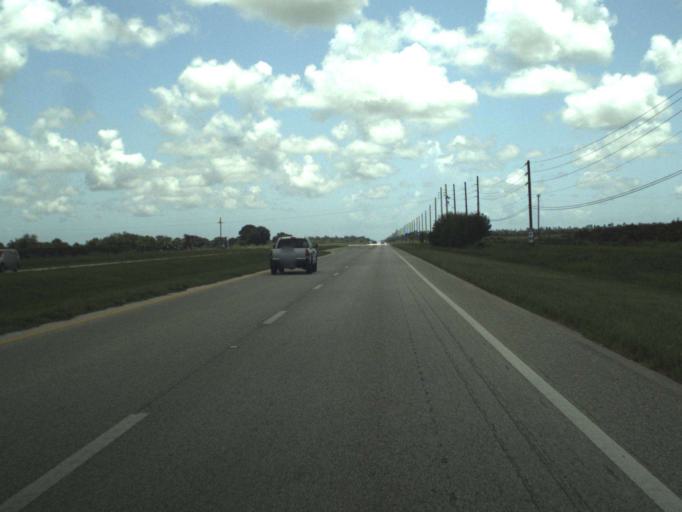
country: US
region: Florida
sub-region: Indian River County
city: West Vero Corridor
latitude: 27.6398
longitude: -80.5982
